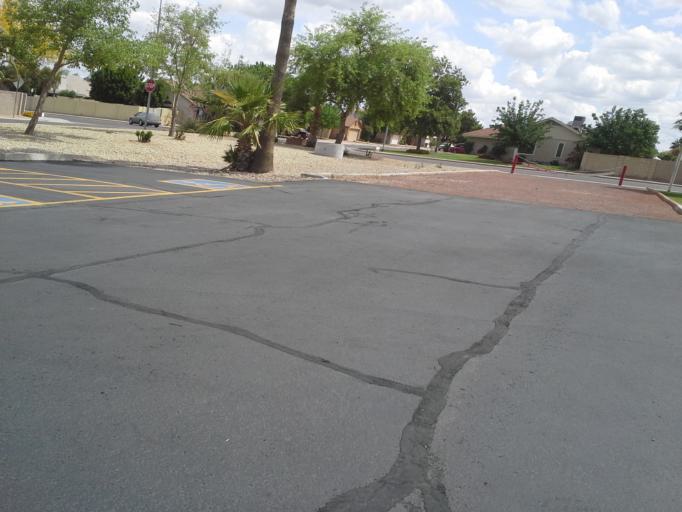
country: US
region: Arizona
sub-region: Maricopa County
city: Peoria
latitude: 33.6136
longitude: -112.2294
